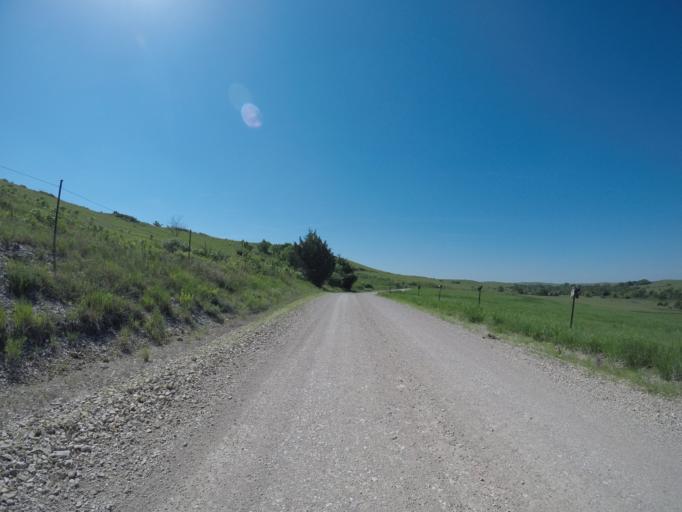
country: US
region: Kansas
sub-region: Wabaunsee County
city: Alma
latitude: 39.0164
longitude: -96.1527
